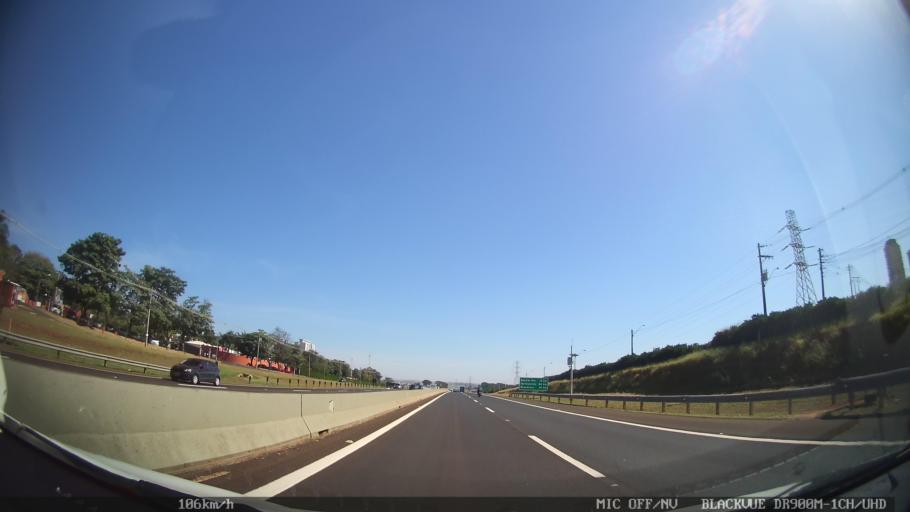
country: BR
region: Sao Paulo
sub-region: Ribeirao Preto
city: Ribeirao Preto
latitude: -21.2238
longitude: -47.8013
